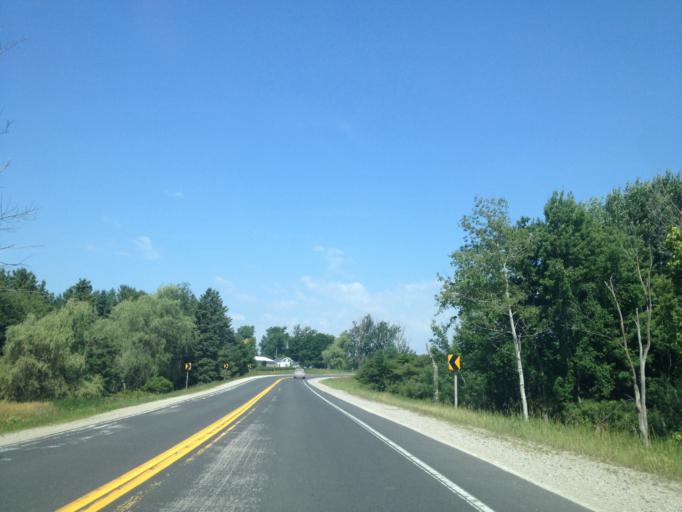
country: CA
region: Ontario
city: Huron East
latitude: 43.3731
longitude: -81.2150
